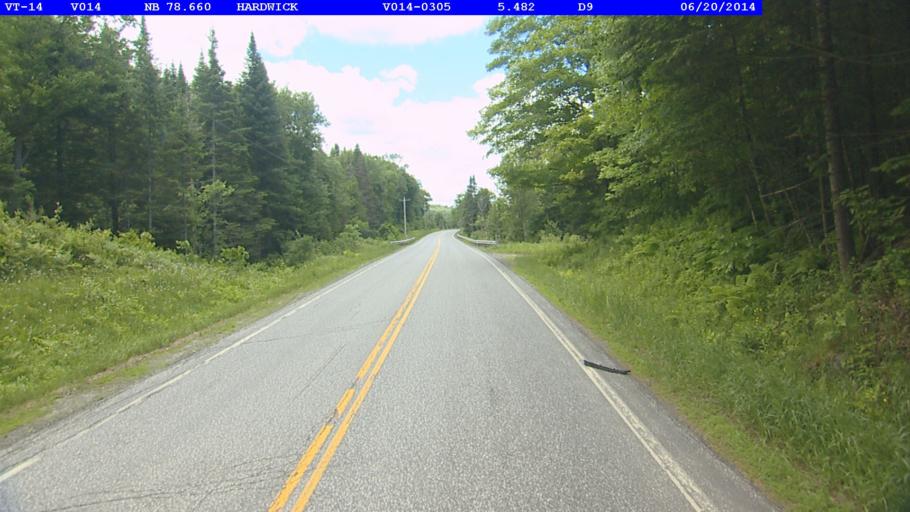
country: US
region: Vermont
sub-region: Caledonia County
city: Hardwick
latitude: 44.5723
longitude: -72.3651
